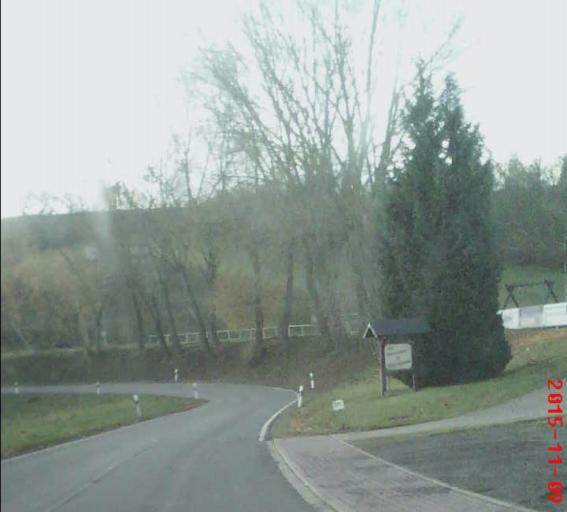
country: DE
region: Thuringia
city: Pfaffschwende
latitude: 51.2456
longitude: 10.0986
